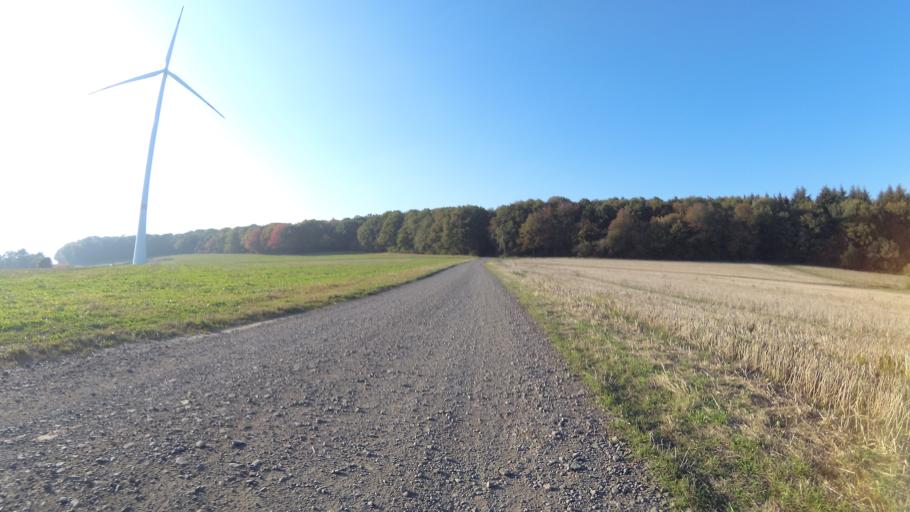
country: DE
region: Saarland
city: Sankt Wendel
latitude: 49.4433
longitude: 7.2041
